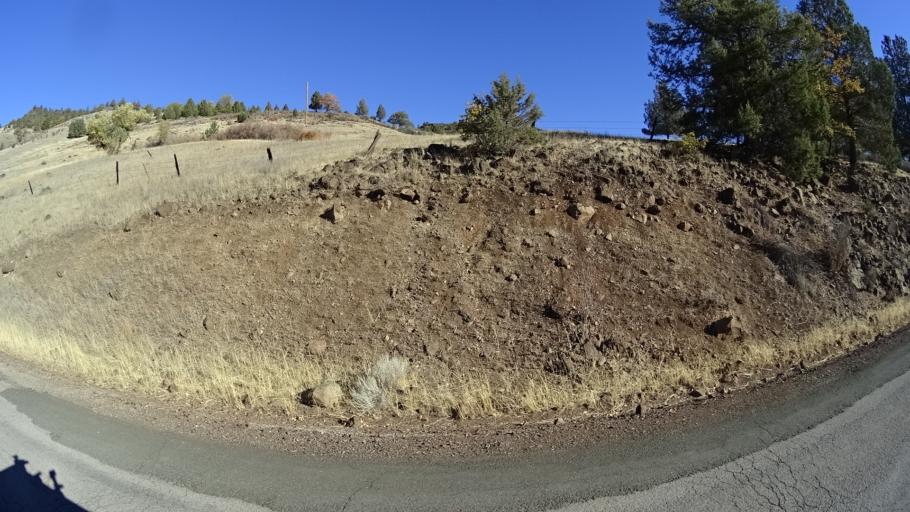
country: US
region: California
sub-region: Siskiyou County
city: Montague
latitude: 41.9692
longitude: -122.3835
